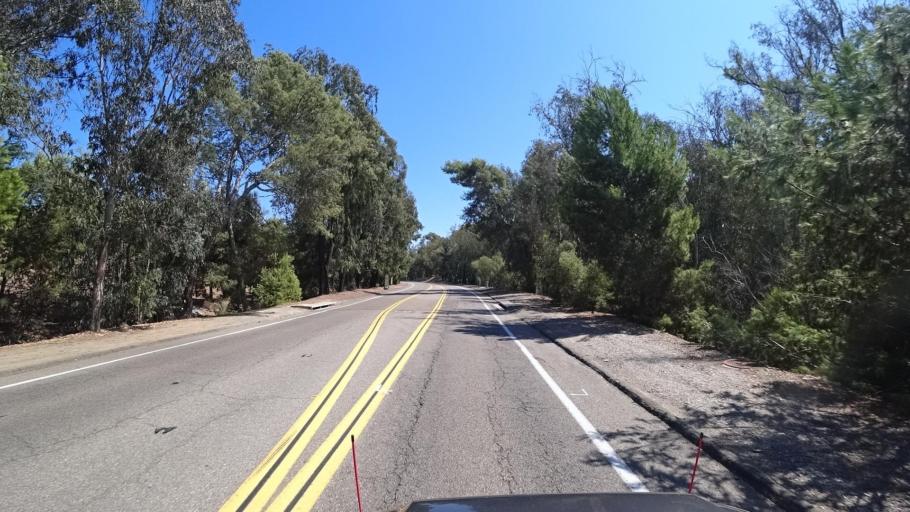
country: US
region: California
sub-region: San Diego County
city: Fairbanks Ranch
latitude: 32.9965
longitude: -117.1868
